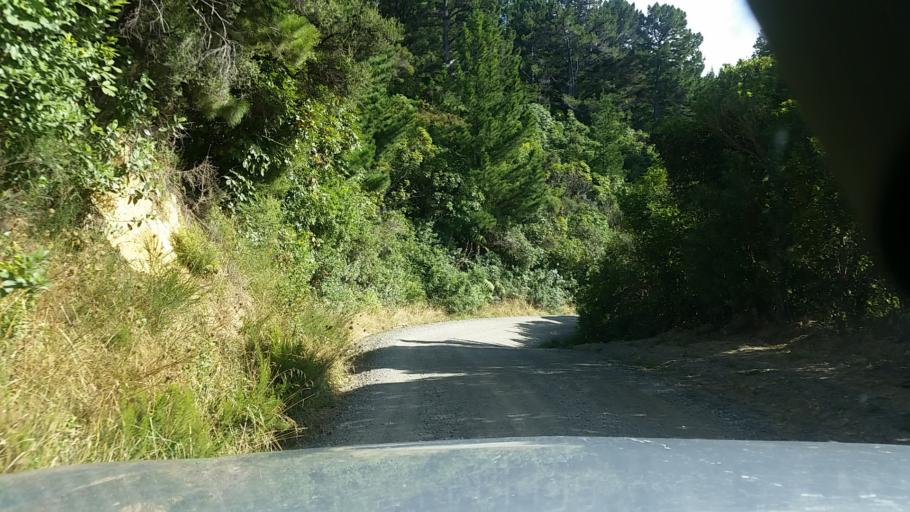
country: NZ
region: Marlborough
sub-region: Marlborough District
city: Picton
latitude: -41.2890
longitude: 174.1309
